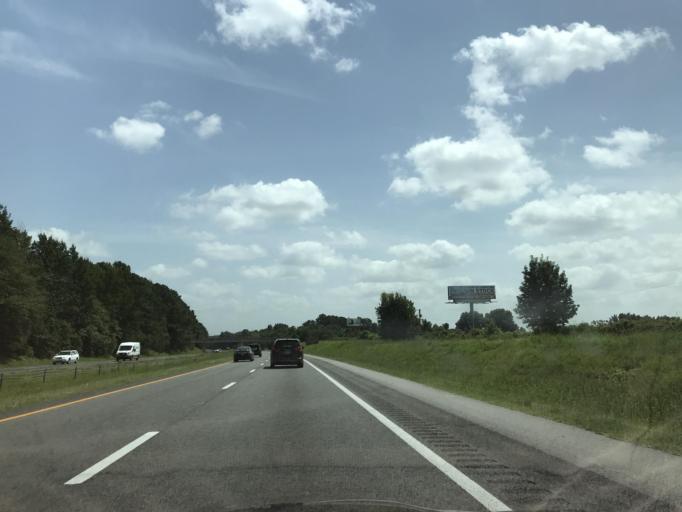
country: US
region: North Carolina
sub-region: Sampson County
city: Plain View
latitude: 35.2356
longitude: -78.3670
